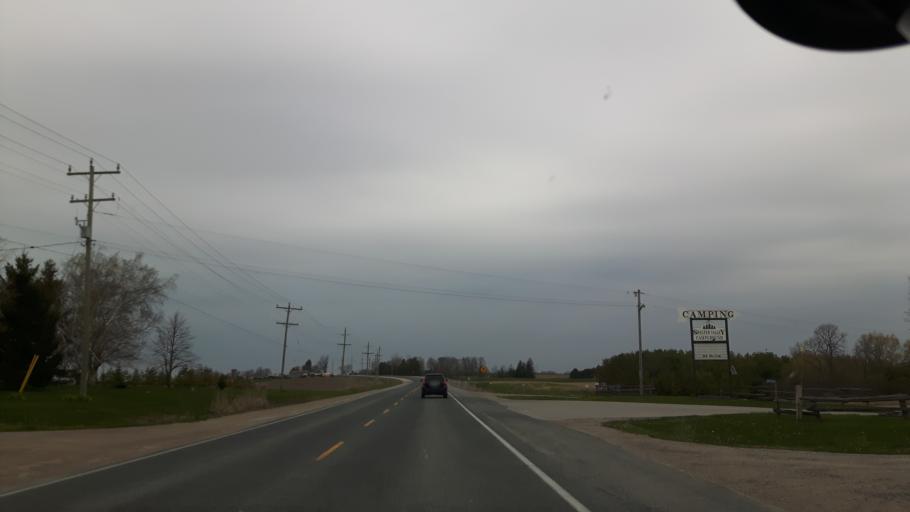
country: CA
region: Ontario
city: Goderich
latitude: 43.6874
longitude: -81.6317
